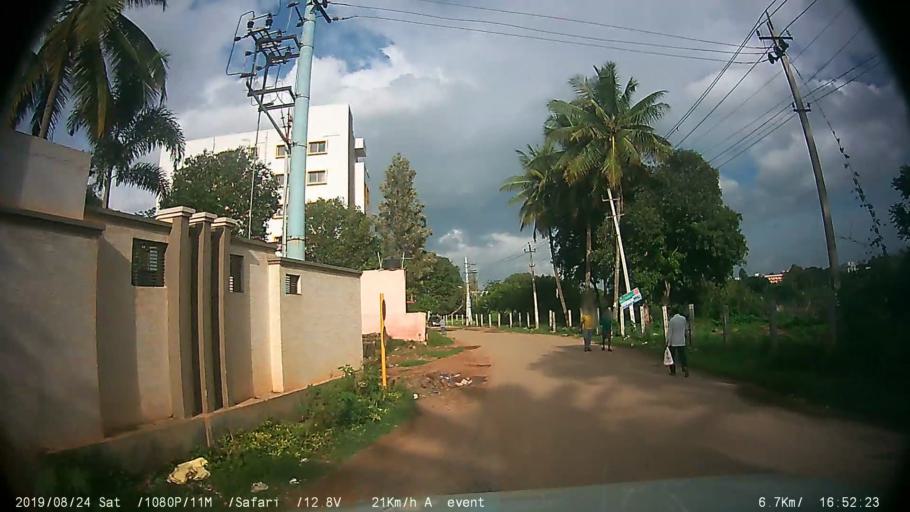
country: IN
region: Karnataka
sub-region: Bangalore Urban
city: Anekal
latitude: 12.8279
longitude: 77.6869
